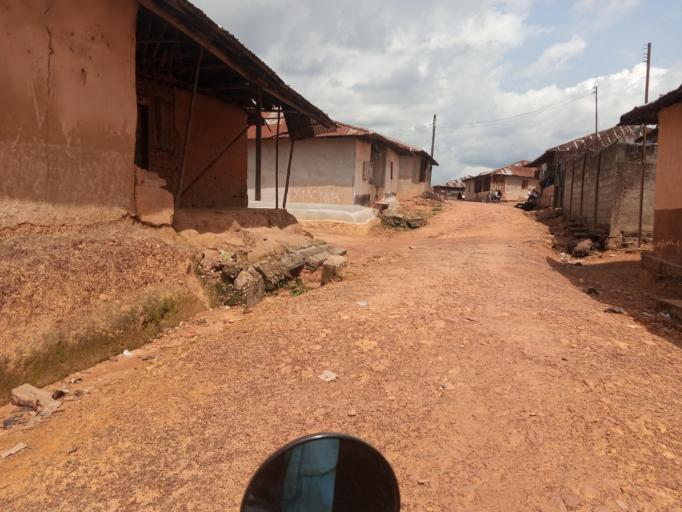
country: SL
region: Southern Province
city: Bo
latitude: 7.9751
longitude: -11.7383
